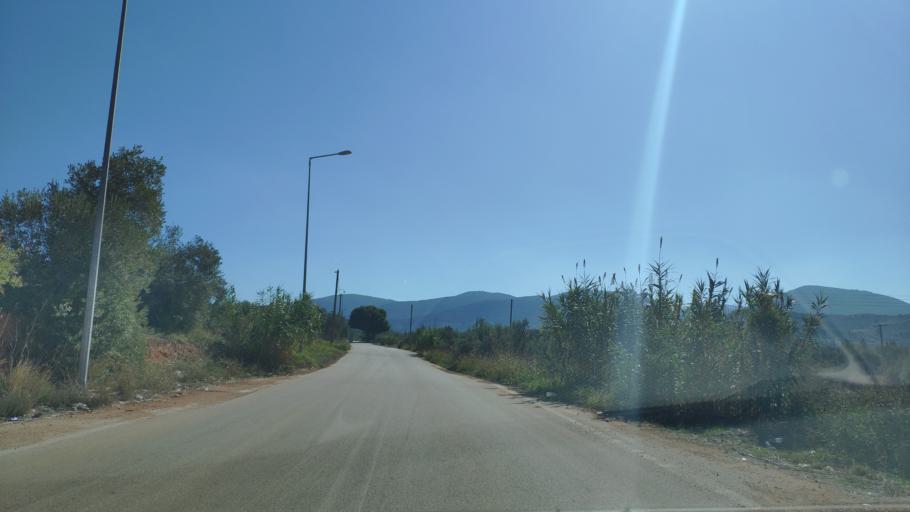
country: GR
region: Peloponnese
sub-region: Nomos Korinthias
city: Athikia
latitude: 37.8473
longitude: 22.9014
